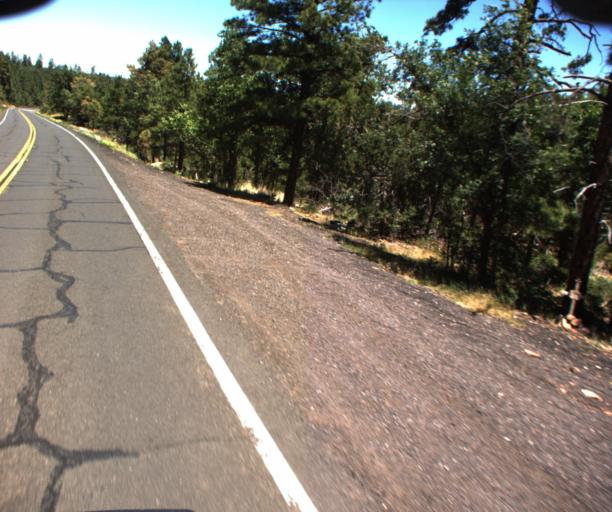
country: US
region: Arizona
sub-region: Gila County
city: Pine
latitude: 34.5992
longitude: -111.2407
